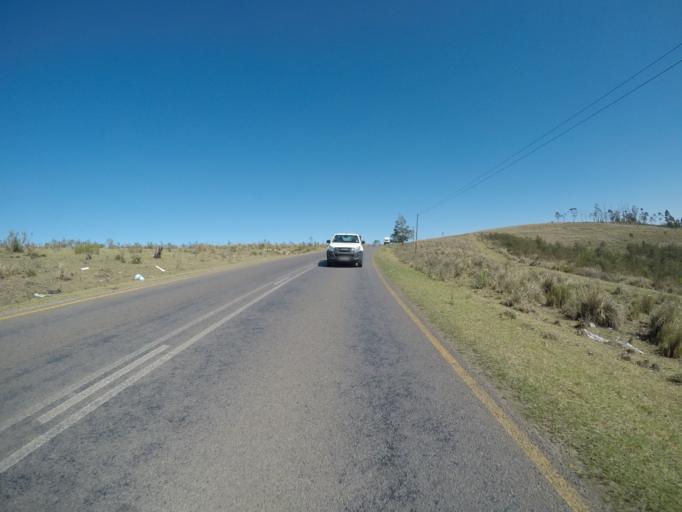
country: ZA
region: Eastern Cape
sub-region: OR Tambo District Municipality
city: Mthatha
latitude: -31.8066
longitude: 28.7570
